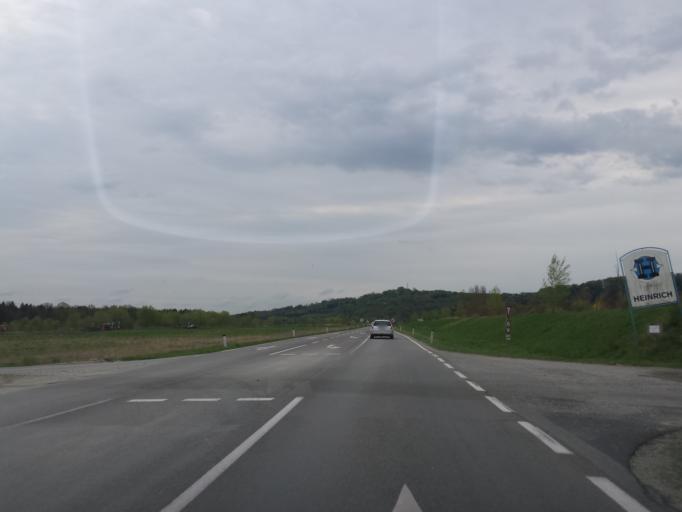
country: AT
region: Styria
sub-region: Politischer Bezirk Hartberg-Fuerstenfeld
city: Soechau
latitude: 47.0715
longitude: 16.0073
